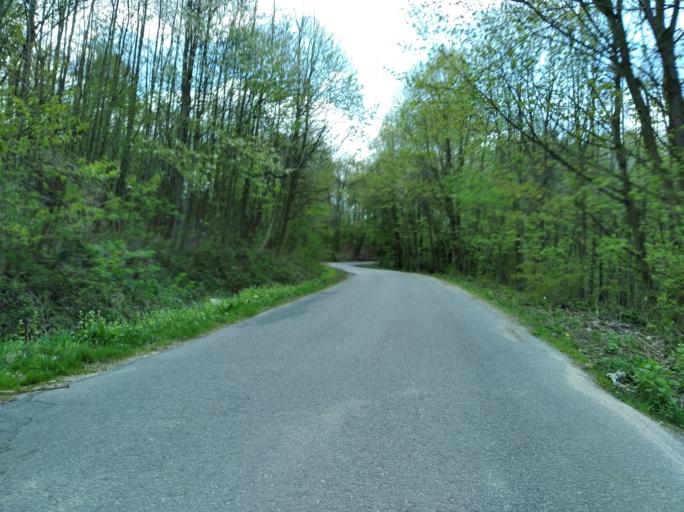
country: PL
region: Subcarpathian Voivodeship
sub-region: Powiat brzozowski
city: Wesola
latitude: 49.7690
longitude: 22.1296
